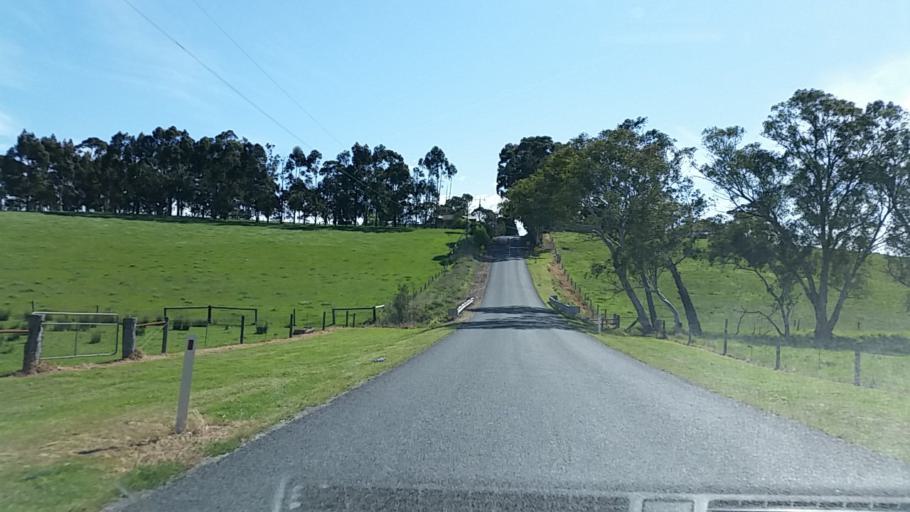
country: AU
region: South Australia
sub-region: Mount Barker
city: Hahndorf
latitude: -35.0772
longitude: 138.8004
